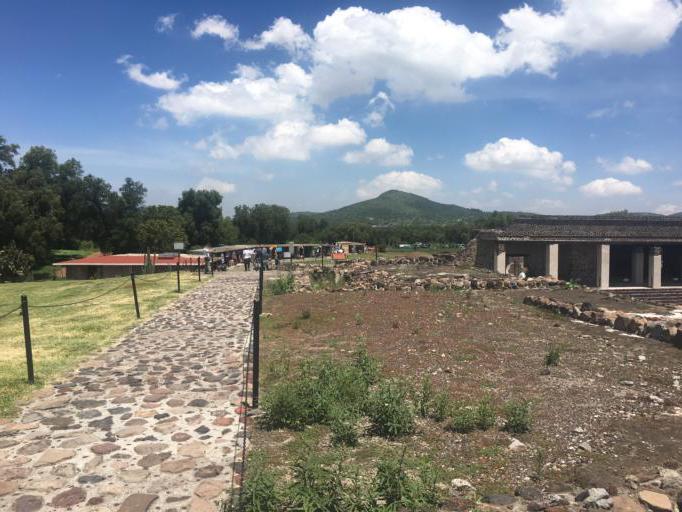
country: MX
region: Morelos
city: San Martin de las Piramides
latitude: 19.6973
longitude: -98.8451
